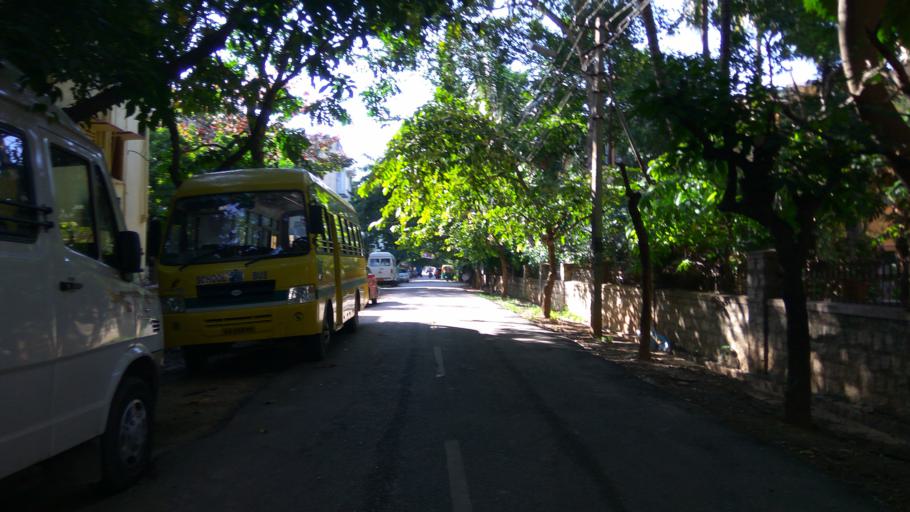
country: IN
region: Karnataka
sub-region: Bangalore Urban
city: Bangalore
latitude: 12.9641
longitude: 77.6366
